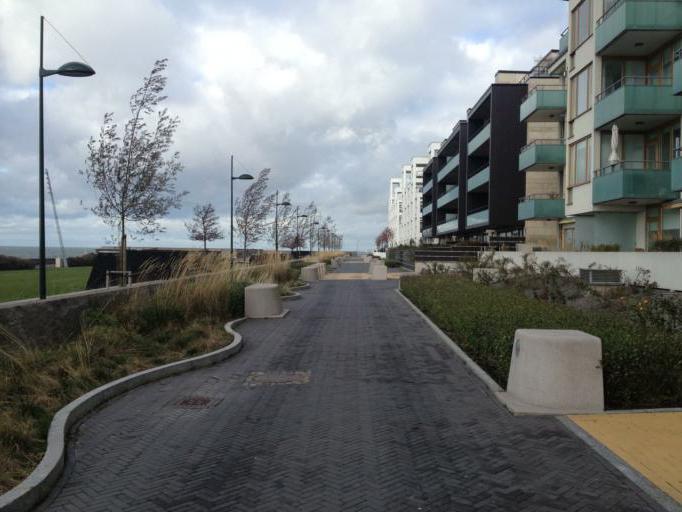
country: SE
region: Skane
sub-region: Malmo
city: Malmoe
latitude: 55.6132
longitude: 12.9728
